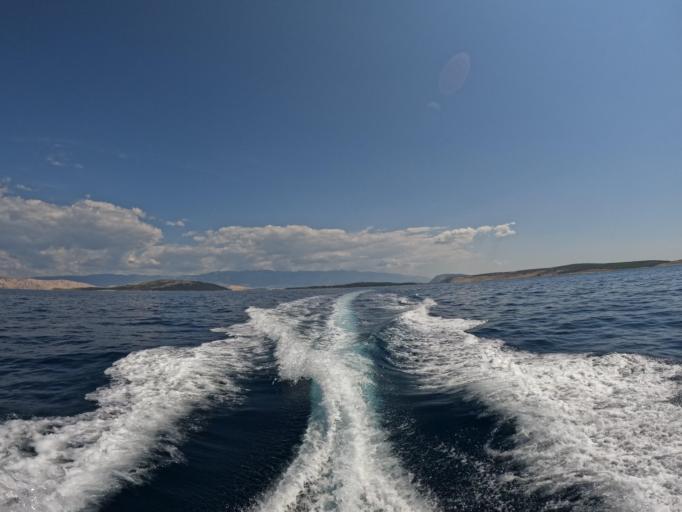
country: HR
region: Primorsko-Goranska
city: Lopar
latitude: 44.8663
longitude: 14.6828
